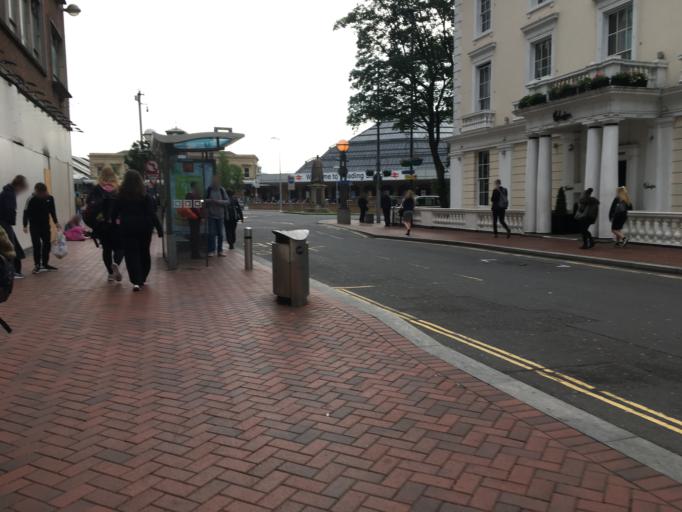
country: GB
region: England
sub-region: Reading
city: Reading
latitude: 51.4575
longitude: -0.9722
